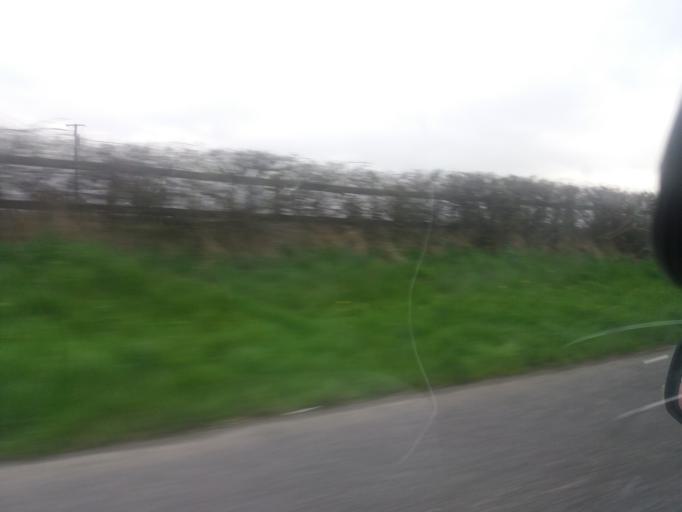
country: IE
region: Munster
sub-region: County Limerick
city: Newcastle West
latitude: 52.4725
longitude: -9.0196
